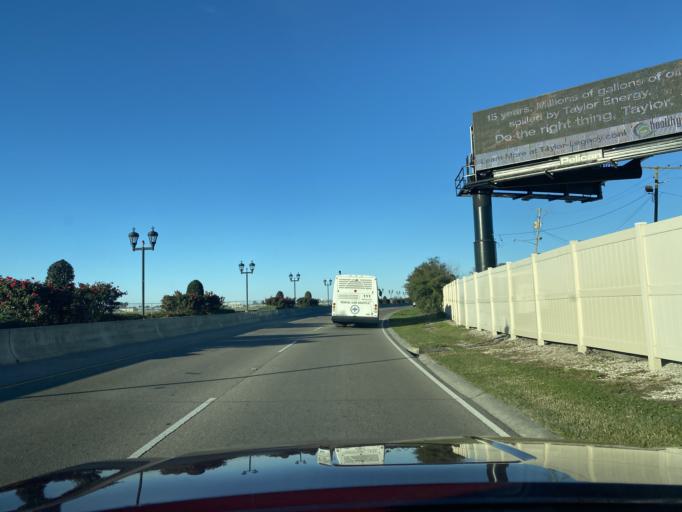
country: US
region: Louisiana
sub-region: Jefferson Parish
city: Kenner
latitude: 29.9908
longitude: -90.2478
